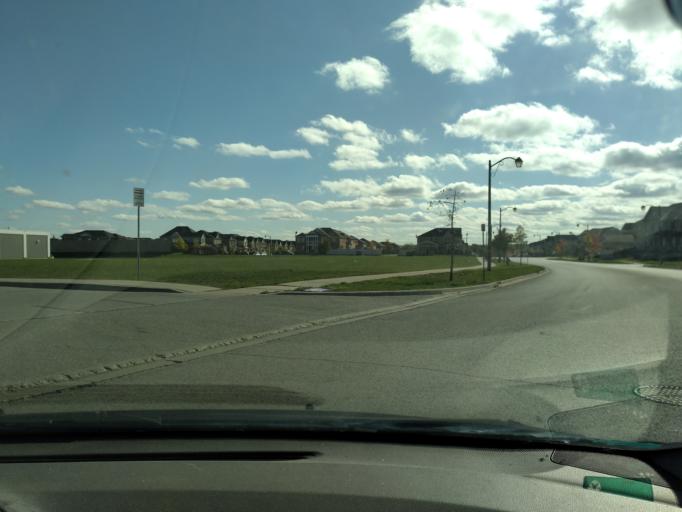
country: CA
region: Ontario
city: Bradford West Gwillimbury
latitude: 44.1063
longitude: -79.5937
